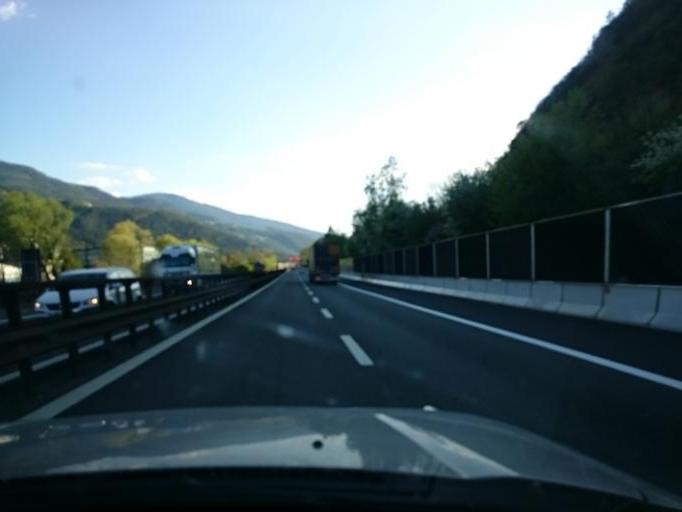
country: IT
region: Trentino-Alto Adige
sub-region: Bolzano
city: Bressanone
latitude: 46.6990
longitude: 11.6450
